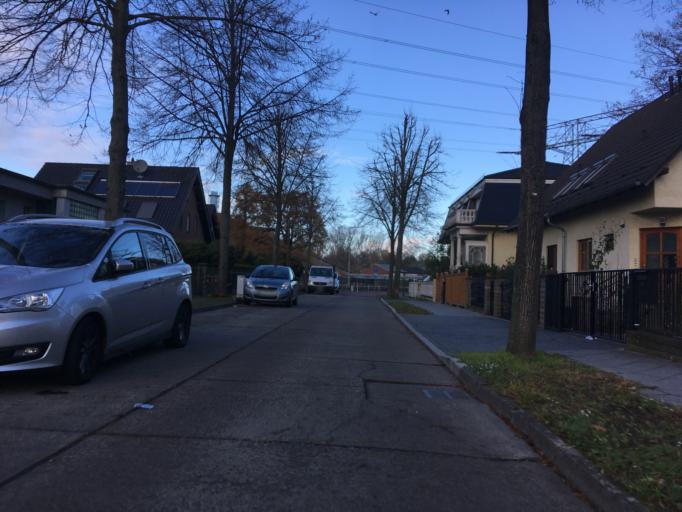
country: DE
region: Berlin
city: Karlshorst
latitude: 52.4953
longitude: 13.5318
